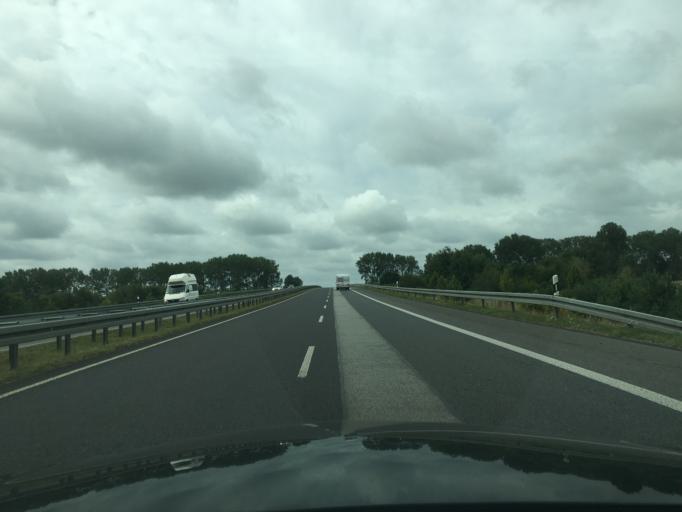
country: DE
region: Brandenburg
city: Oranienburg
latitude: 52.7788
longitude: 13.2225
